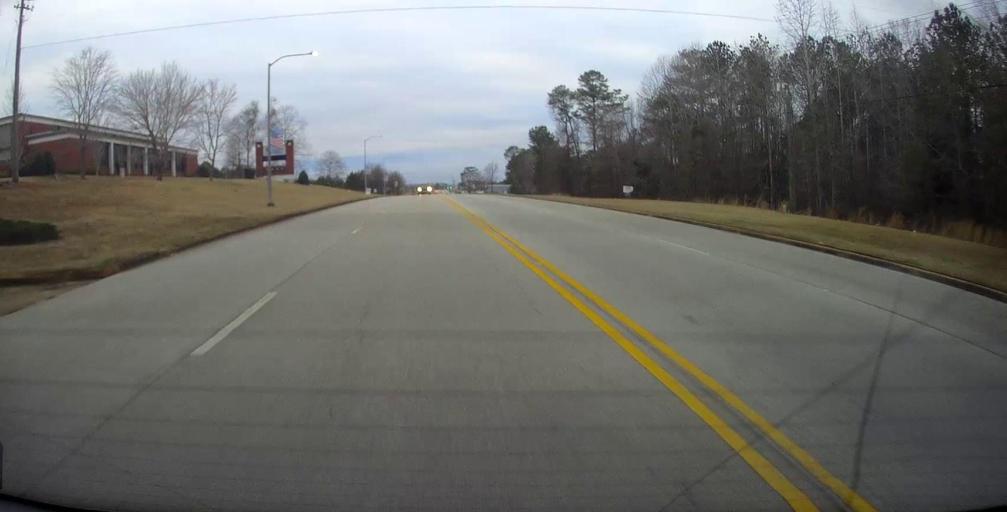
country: US
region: Alabama
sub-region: Chambers County
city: Valley
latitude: 32.8176
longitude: -85.1937
